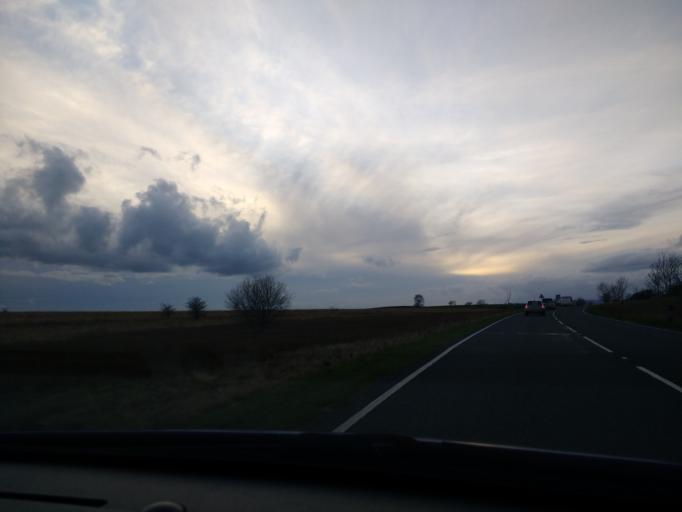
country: GB
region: England
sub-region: North Yorkshire
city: Ingleton
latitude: 54.1273
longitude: -2.4400
